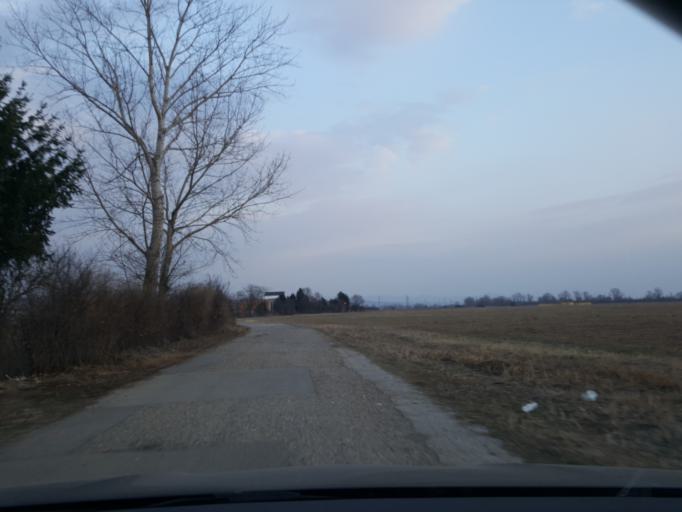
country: RS
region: Central Serbia
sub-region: Nisavski Okrug
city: Aleksinac
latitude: 43.5521
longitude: 21.6661
